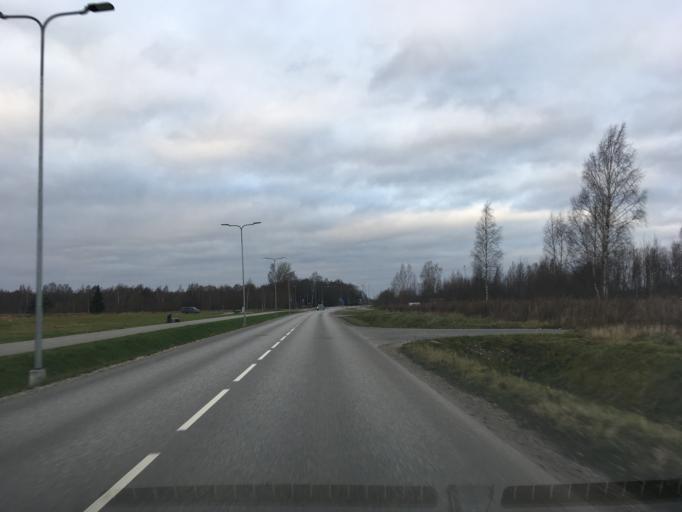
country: EE
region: Paernumaa
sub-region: Paernu linn
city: Parnu
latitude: 58.4008
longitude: 24.4779
